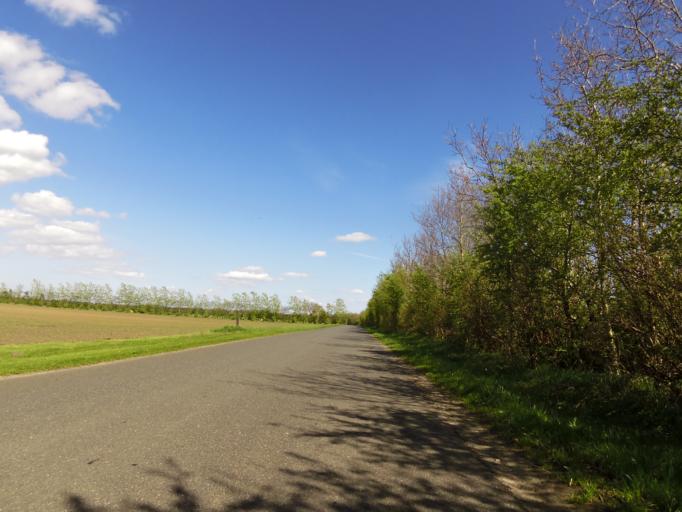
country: DK
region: Central Jutland
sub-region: Skive Kommune
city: Skive
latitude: 56.4596
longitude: 8.9655
